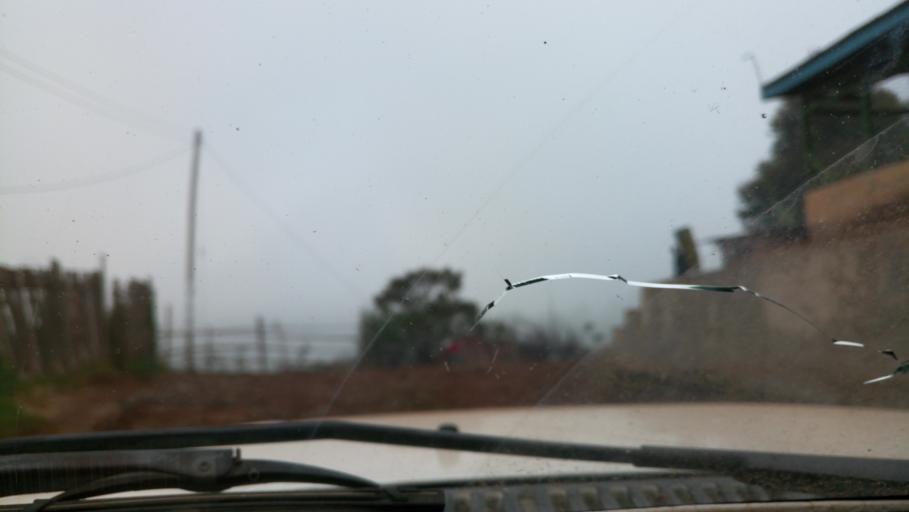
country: KE
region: Murang'a District
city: Kangema
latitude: -0.6614
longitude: 36.8268
